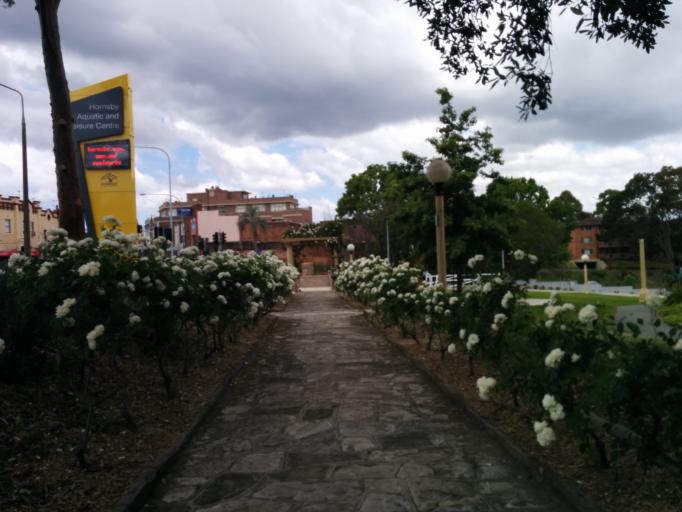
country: AU
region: New South Wales
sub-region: Hornsby Shire
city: Hornsby
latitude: -33.7015
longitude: 151.0967
